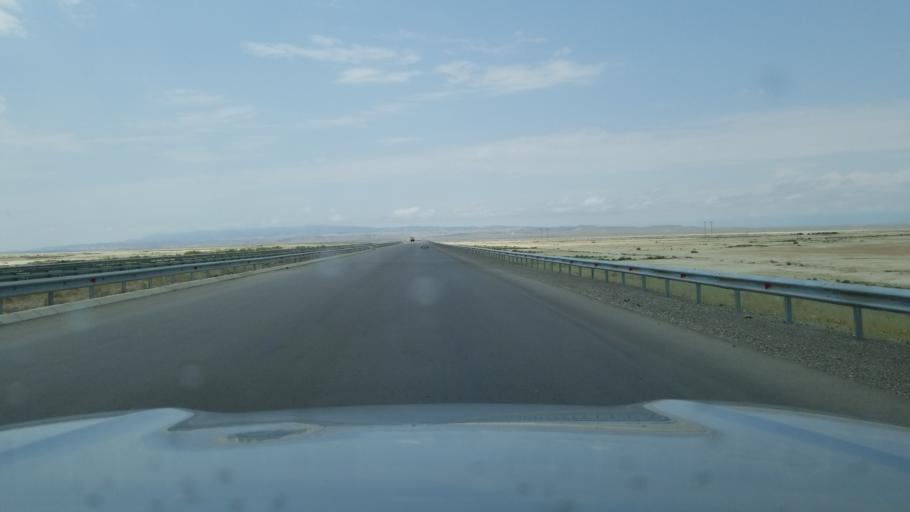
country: TM
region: Balkan
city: Gazanjyk
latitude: 39.2811
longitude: 55.2464
